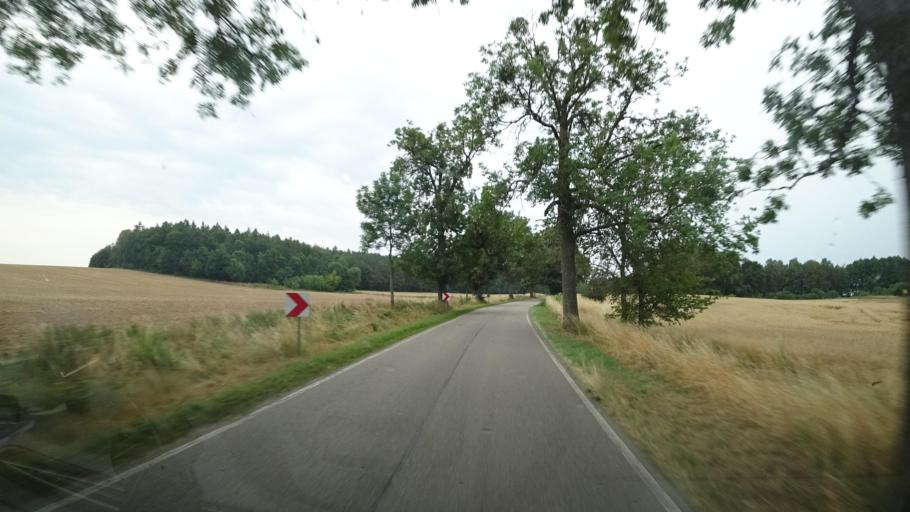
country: PL
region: Warmian-Masurian Voivodeship
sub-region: Powiat gizycki
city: Ryn
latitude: 53.8986
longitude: 21.5717
